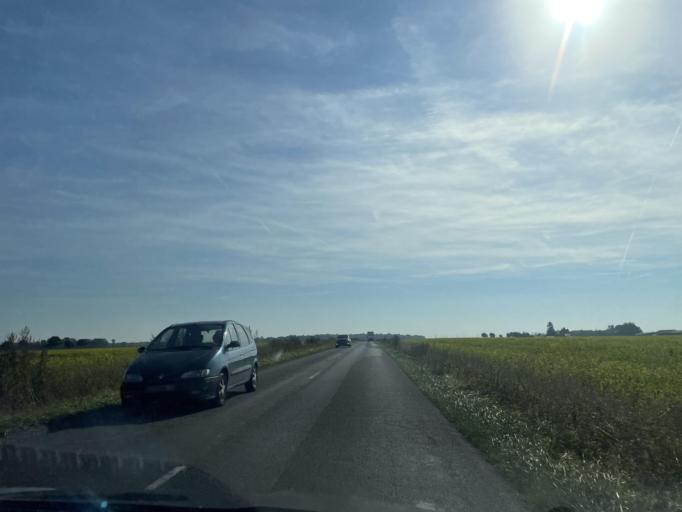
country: FR
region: Ile-de-France
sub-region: Departement de Seine-et-Marne
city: Coulommiers
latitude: 48.8725
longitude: 3.0857
